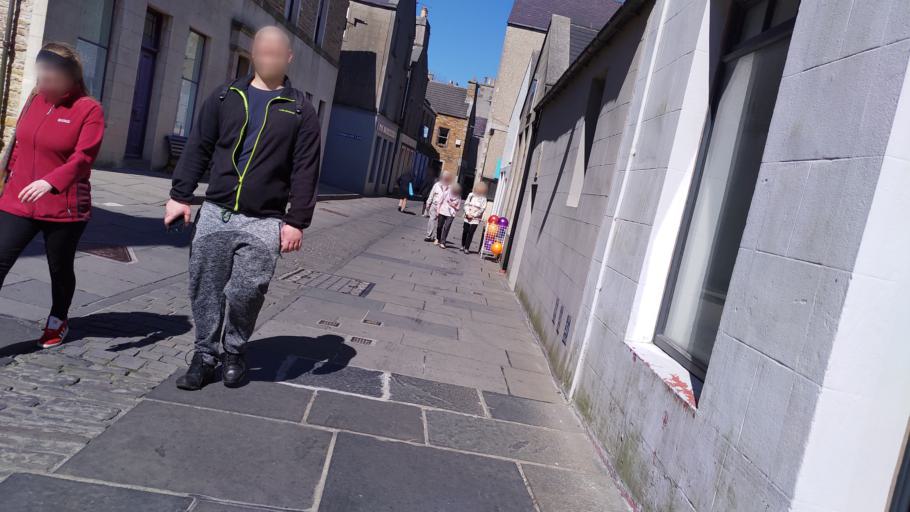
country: GB
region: Scotland
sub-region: Orkney Islands
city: Stromness
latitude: 58.9621
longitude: -3.2992
